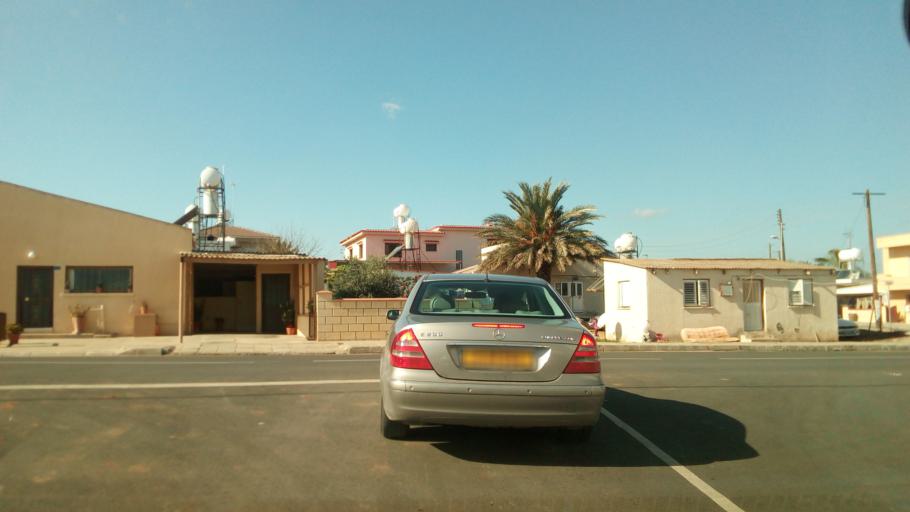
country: CY
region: Ammochostos
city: Avgorou
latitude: 34.9754
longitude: 33.8405
